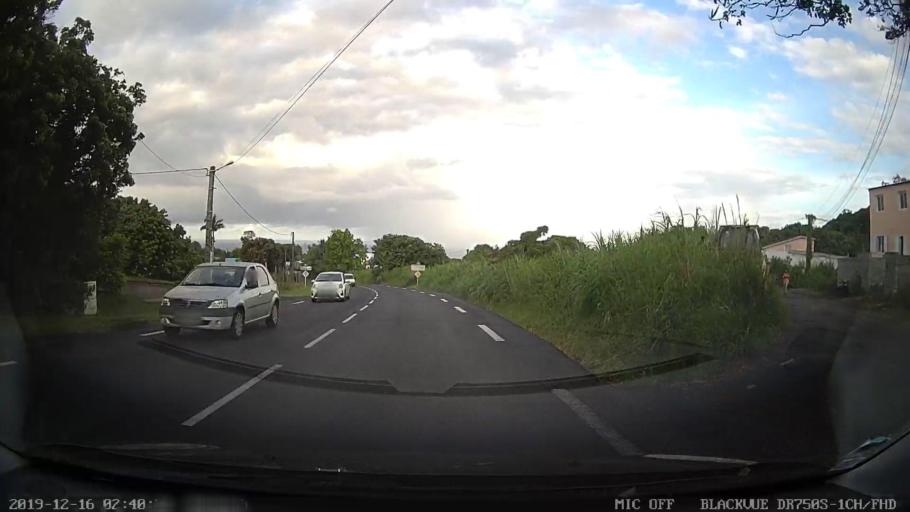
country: RE
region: Reunion
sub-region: Reunion
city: Saint-Benoit
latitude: -21.0735
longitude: 55.7013
